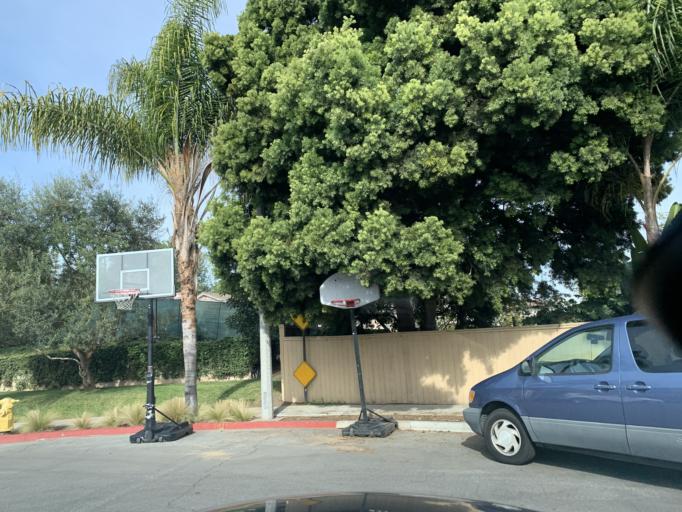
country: US
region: California
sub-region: Los Angeles County
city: Hermosa Beach
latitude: 33.8764
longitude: -118.3929
